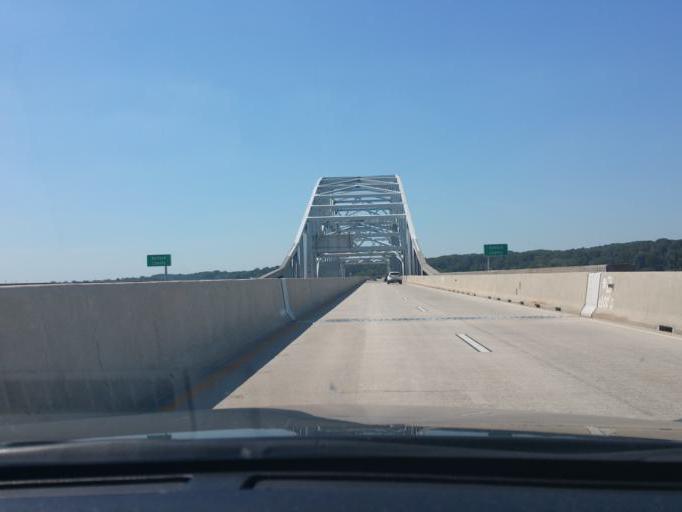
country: US
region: Maryland
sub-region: Harford County
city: Havre de Grace
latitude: 39.5614
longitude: -76.0885
